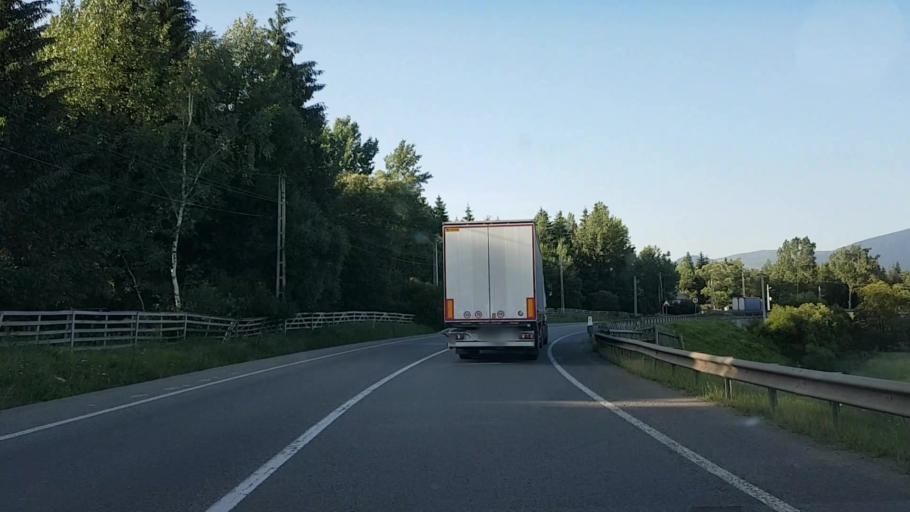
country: RO
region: Suceava
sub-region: Comuna Poiana Stampei
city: Poiana Stampei
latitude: 47.3361
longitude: 25.1641
